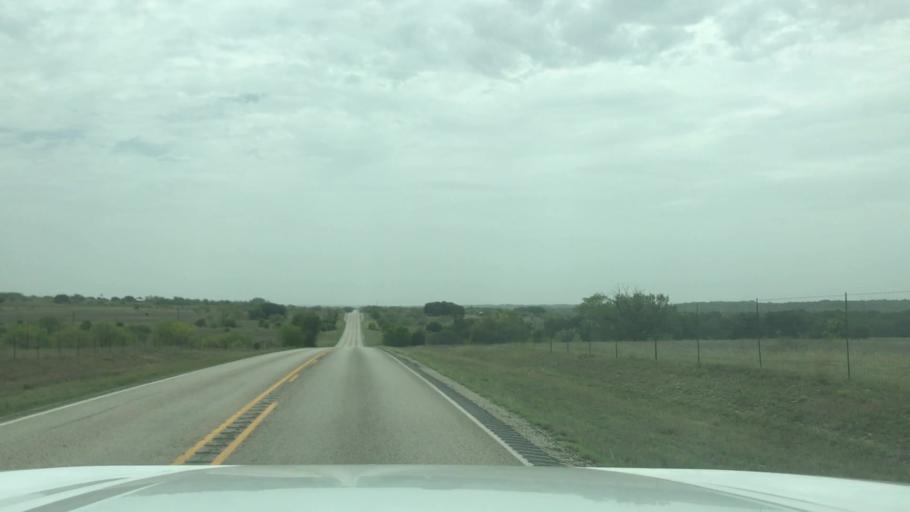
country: US
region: Texas
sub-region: Hamilton County
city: Hico
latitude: 32.0530
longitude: -98.1711
